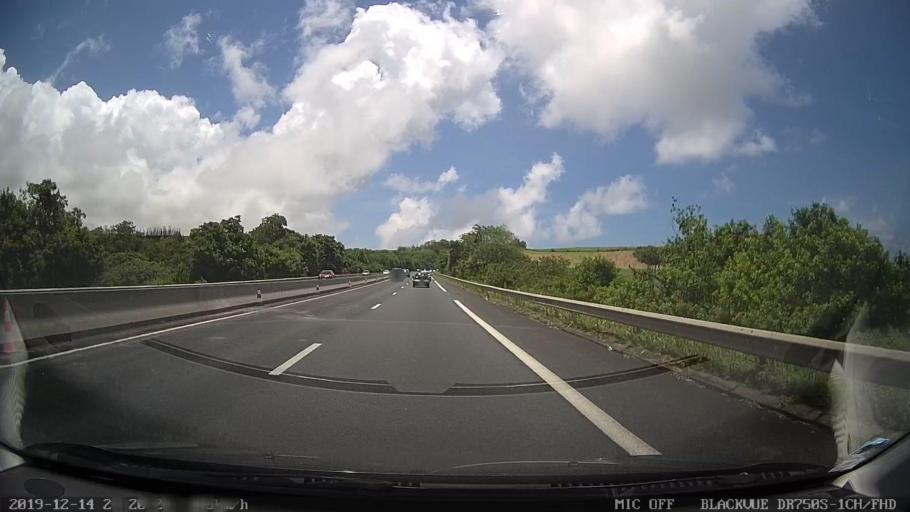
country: RE
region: Reunion
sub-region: Reunion
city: Sainte-Suzanne
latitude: -20.9132
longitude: 55.6094
